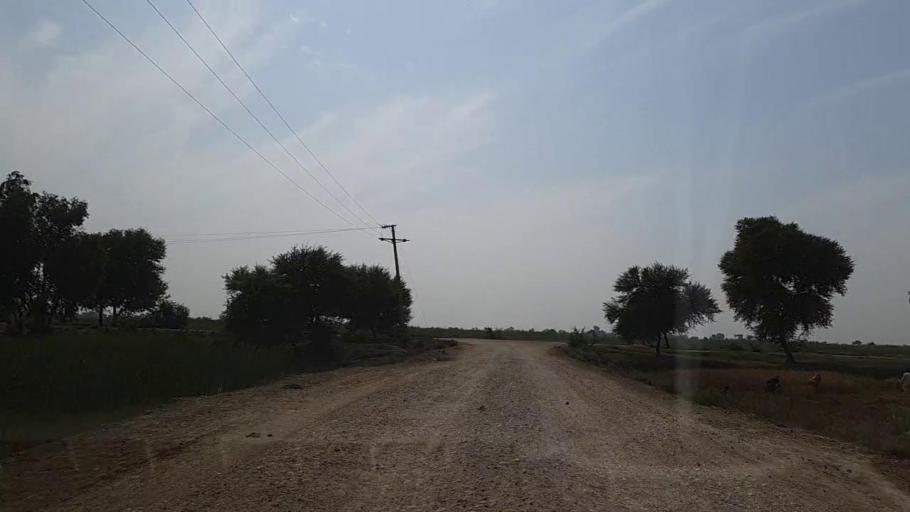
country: PK
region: Sindh
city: Mirpur Batoro
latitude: 24.6115
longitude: 68.2364
